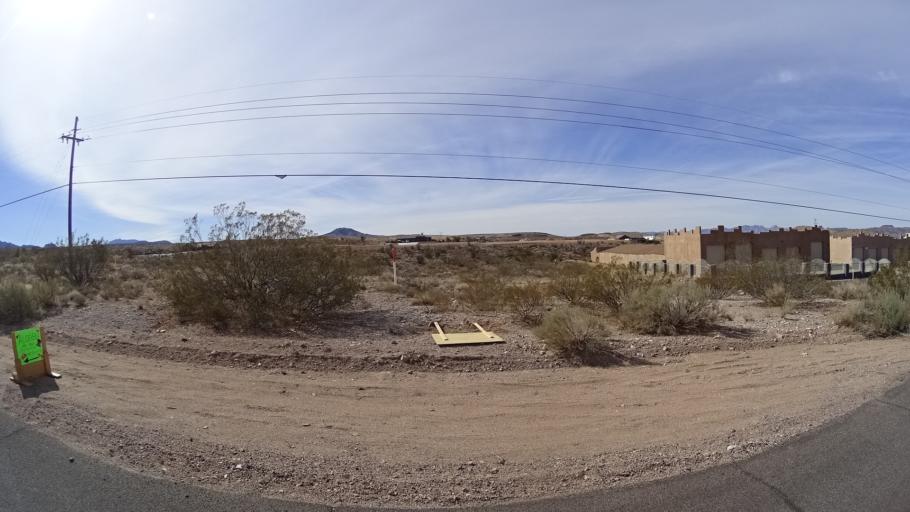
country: US
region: Arizona
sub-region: Mohave County
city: Kingman
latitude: 35.1802
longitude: -113.9951
